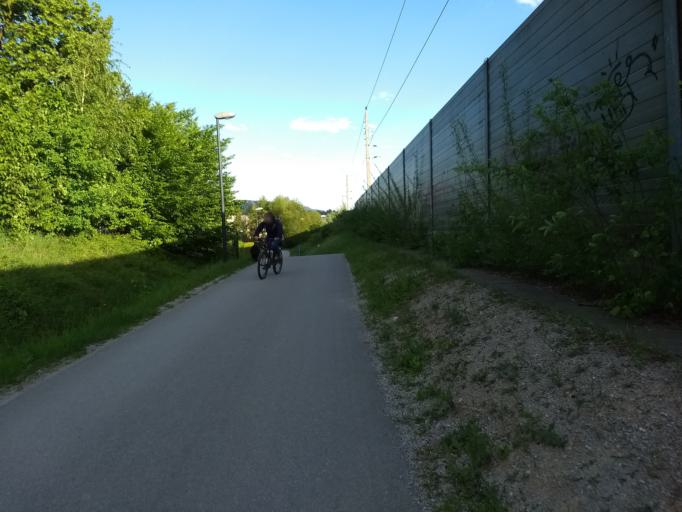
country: AT
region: Salzburg
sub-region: Politischer Bezirk Salzburg-Umgebung
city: Bergheim
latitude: 47.8117
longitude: 13.0165
